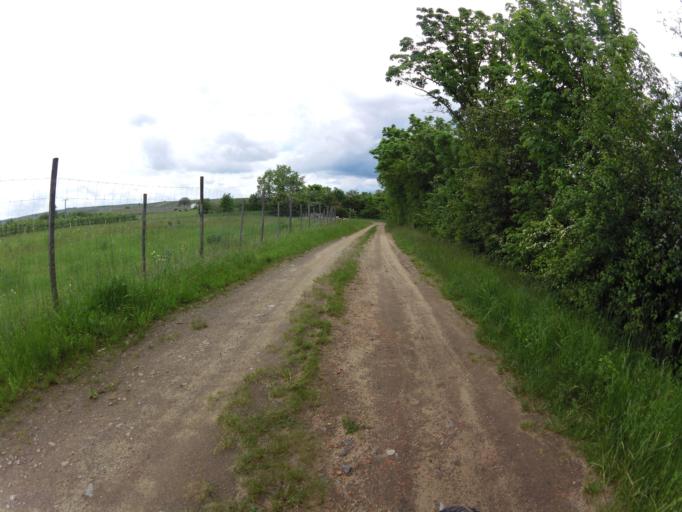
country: DE
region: Bavaria
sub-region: Regierungsbezirk Unterfranken
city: Sommerach
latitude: 49.8258
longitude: 10.2205
